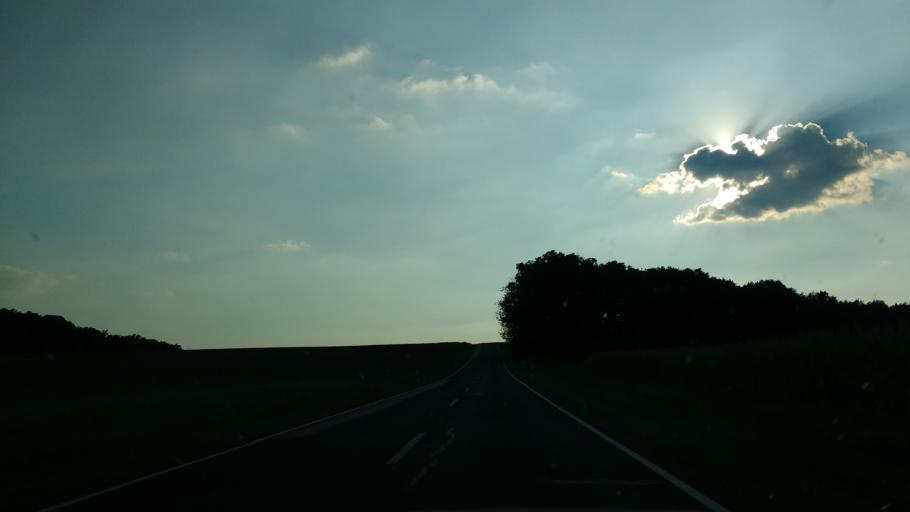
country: DE
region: Bavaria
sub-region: Regierungsbezirk Unterfranken
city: Oberthulba
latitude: 50.1892
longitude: 9.9721
